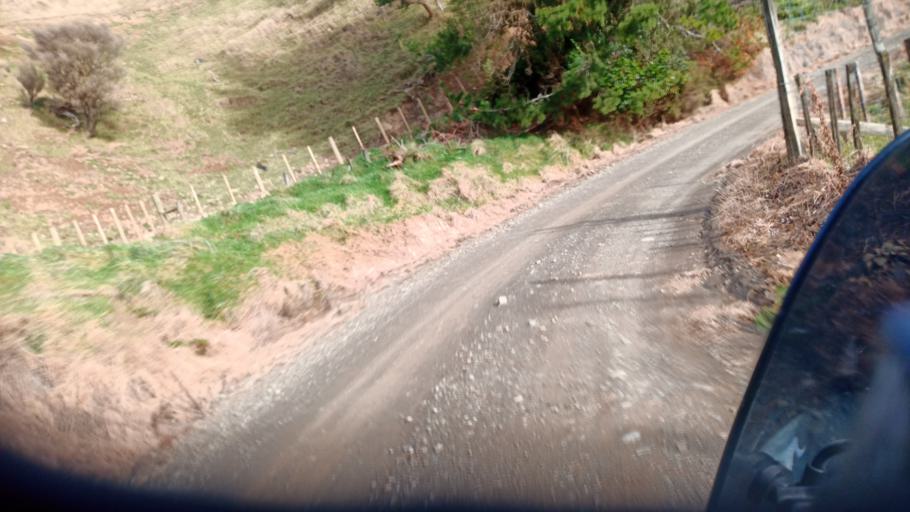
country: NZ
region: Gisborne
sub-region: Gisborne District
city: Gisborne
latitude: -38.4590
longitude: 177.5393
